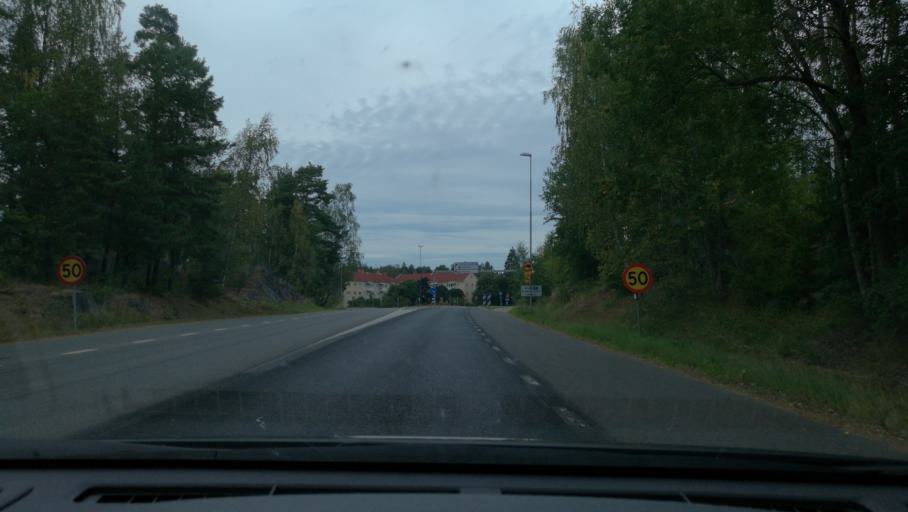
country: SE
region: Soedermanland
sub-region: Katrineholms Kommun
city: Katrineholm
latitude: 58.9850
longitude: 16.2091
